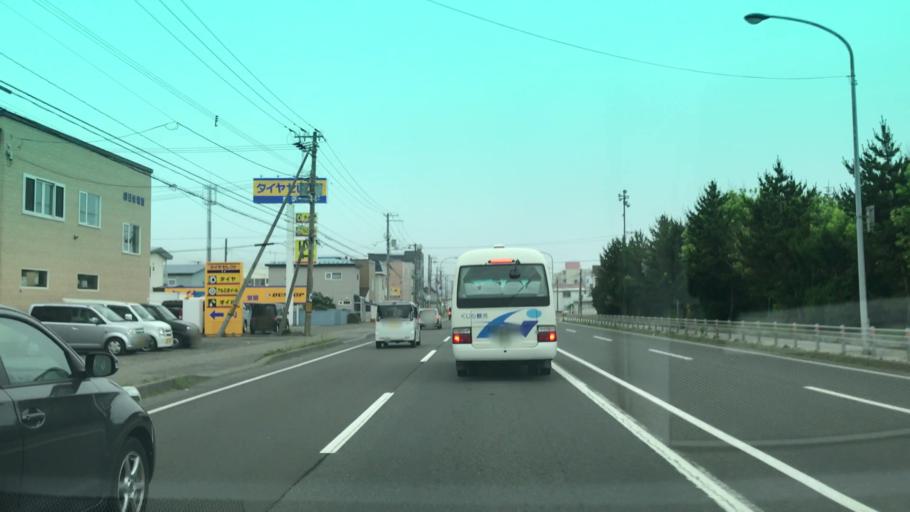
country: JP
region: Hokkaido
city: Muroran
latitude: 42.3604
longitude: 141.0537
